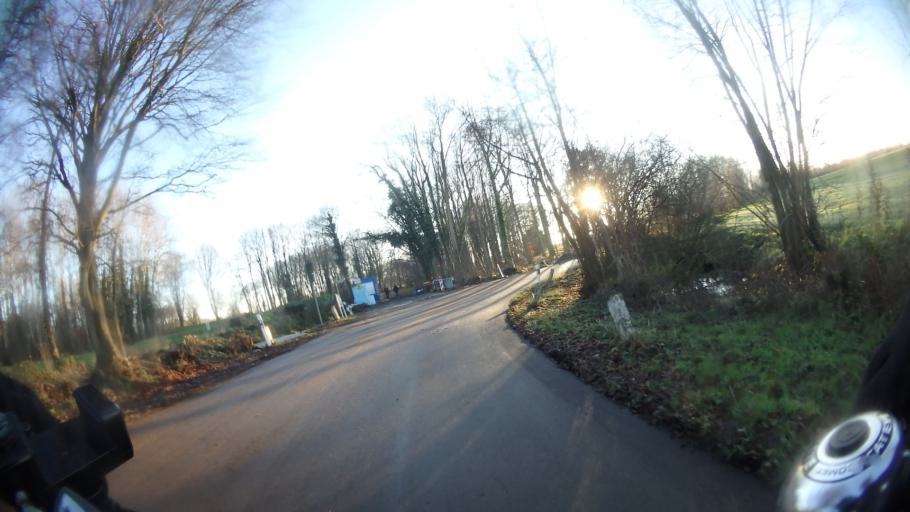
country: DE
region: Schleswig-Holstein
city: Travemuende
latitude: 53.9847
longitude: 10.8725
